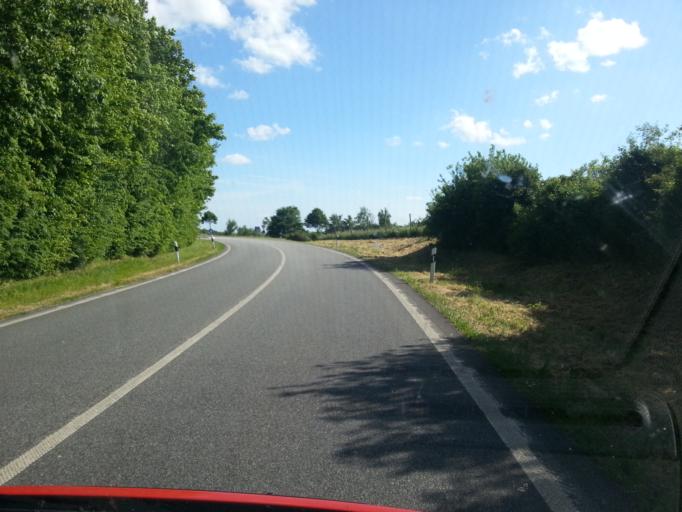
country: DE
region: Schleswig-Holstein
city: Scharbeutz
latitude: 54.0063
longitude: 10.7273
